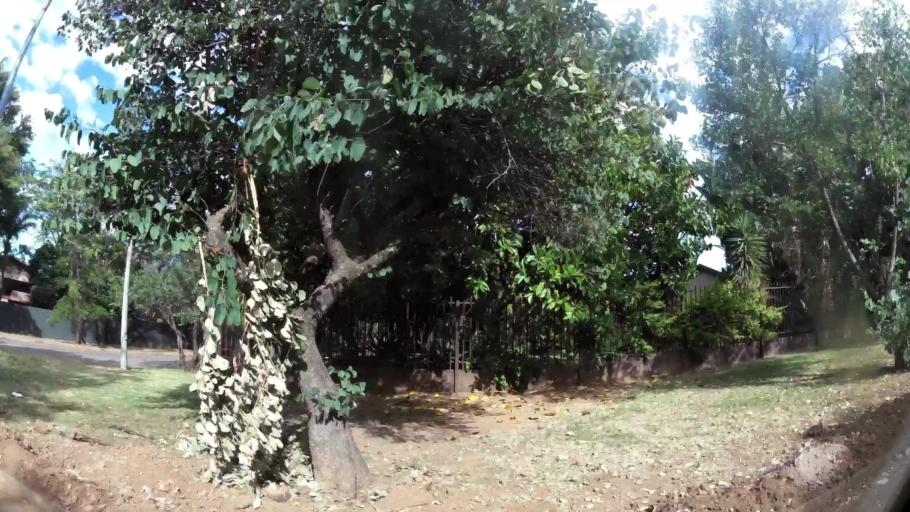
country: ZA
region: Limpopo
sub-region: Waterberg District Municipality
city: Bela-Bela
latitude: -24.8786
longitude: 28.2923
